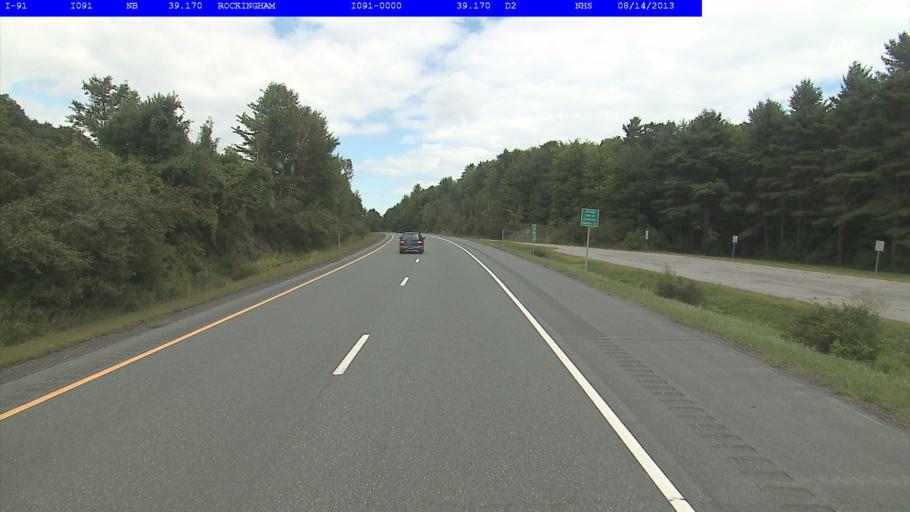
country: US
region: New Hampshire
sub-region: Sullivan County
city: Charlestown
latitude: 43.2331
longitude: -72.4478
